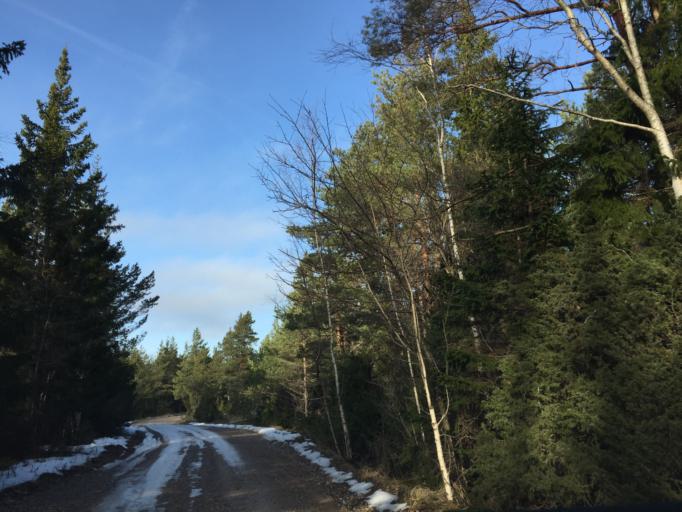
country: EE
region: Saare
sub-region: Kuressaare linn
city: Kuressaare
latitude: 58.4787
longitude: 21.9505
